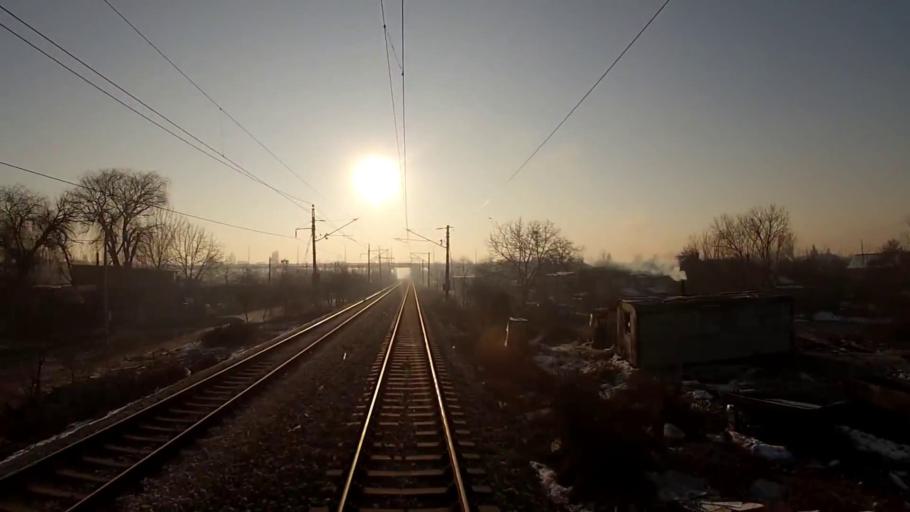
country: BG
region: Sofiya
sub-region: Obshtina Bozhurishte
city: Bozhurishte
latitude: 42.7370
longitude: 23.2655
